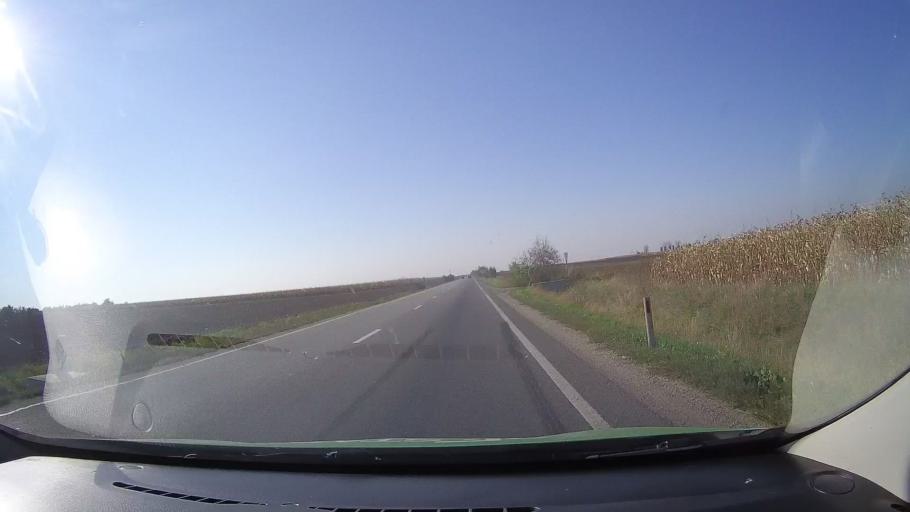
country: RO
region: Satu Mare
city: Carei
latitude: 47.6711
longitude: 22.4413
